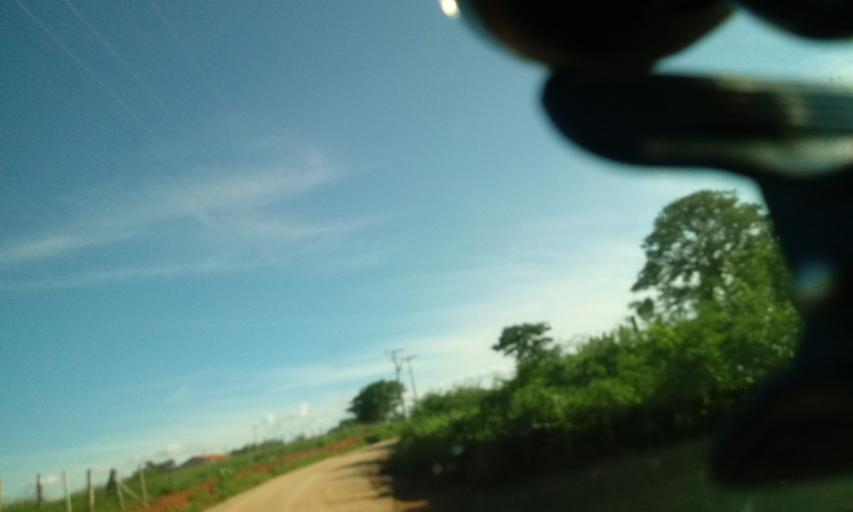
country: BR
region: Bahia
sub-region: Riacho De Santana
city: Riacho de Santana
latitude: -13.8376
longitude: -42.7683
